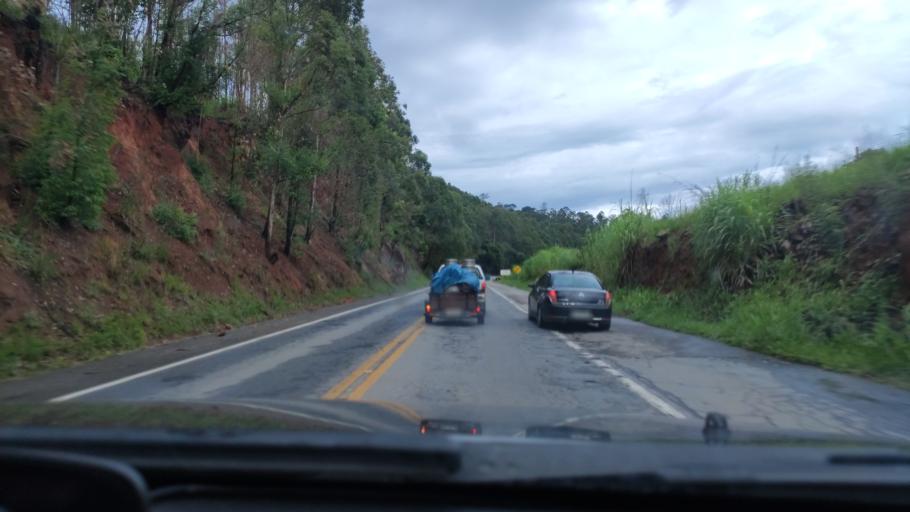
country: BR
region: Sao Paulo
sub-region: Braganca Paulista
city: Braganca Paulista
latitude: -22.8319
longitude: -46.5579
